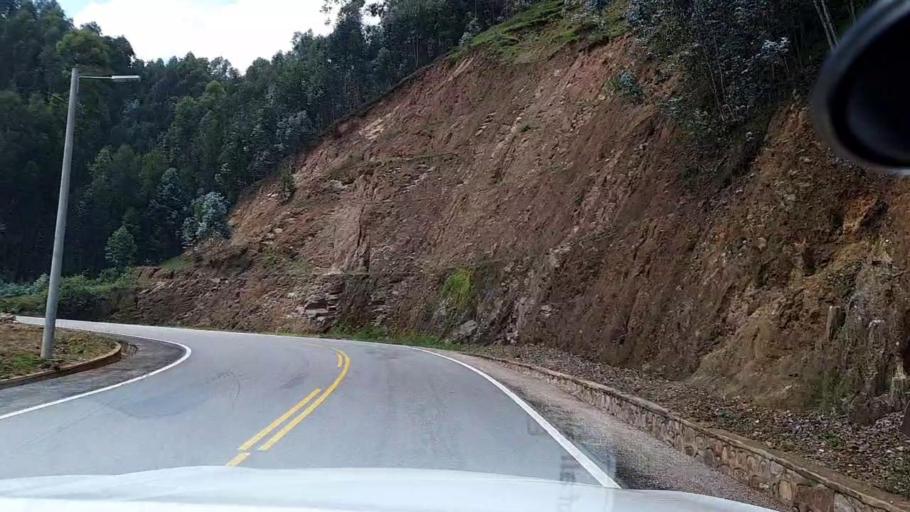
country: RW
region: Southern Province
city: Nzega
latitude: -2.5120
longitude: 29.4620
